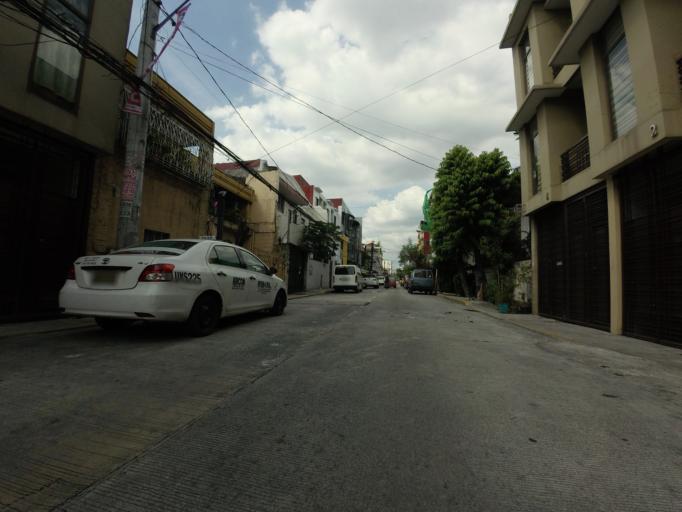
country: PH
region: Metro Manila
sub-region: Makati City
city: Makati City
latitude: 14.5698
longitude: 121.0042
